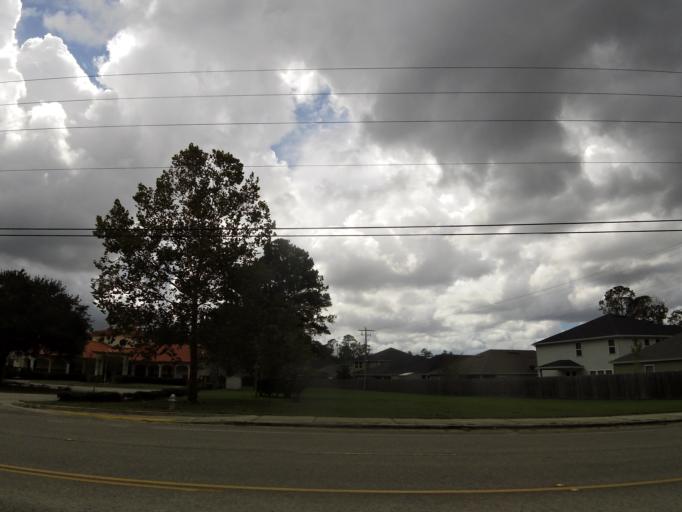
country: US
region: Florida
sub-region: Clay County
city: Lakeside
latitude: 30.1045
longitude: -81.7918
